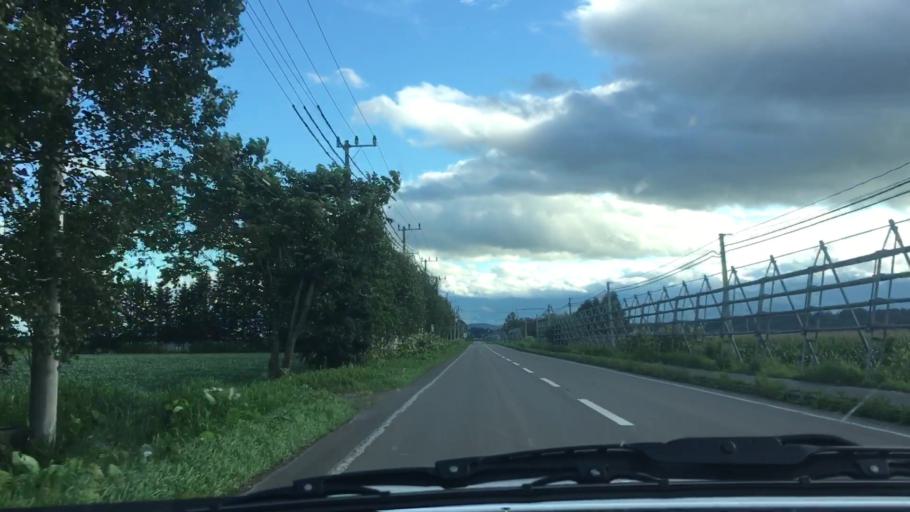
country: JP
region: Hokkaido
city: Otofuke
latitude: 43.1421
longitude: 142.8964
